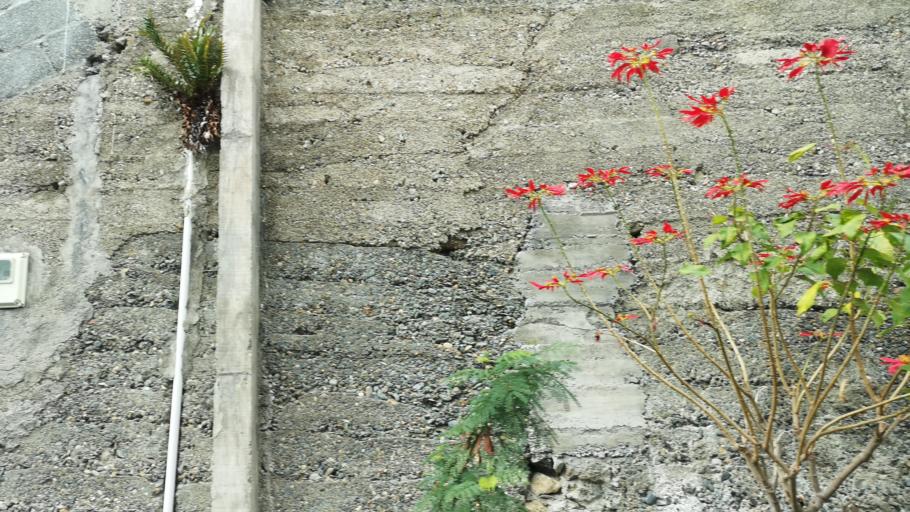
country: ES
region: Canary Islands
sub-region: Provincia de Santa Cruz de Tenerife
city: Vallehermosa
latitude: 28.1788
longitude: -17.2687
